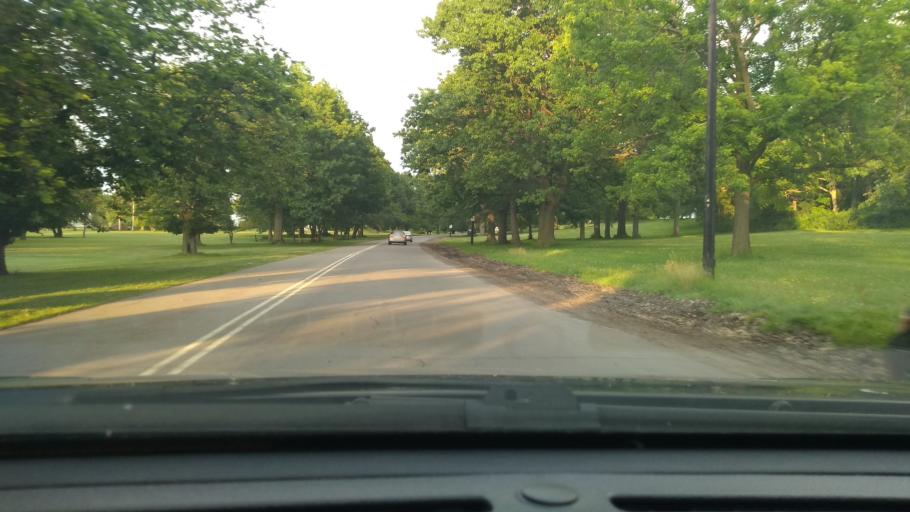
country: US
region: New York
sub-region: Erie County
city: Lackawanna
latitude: 42.8275
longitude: -78.8300
